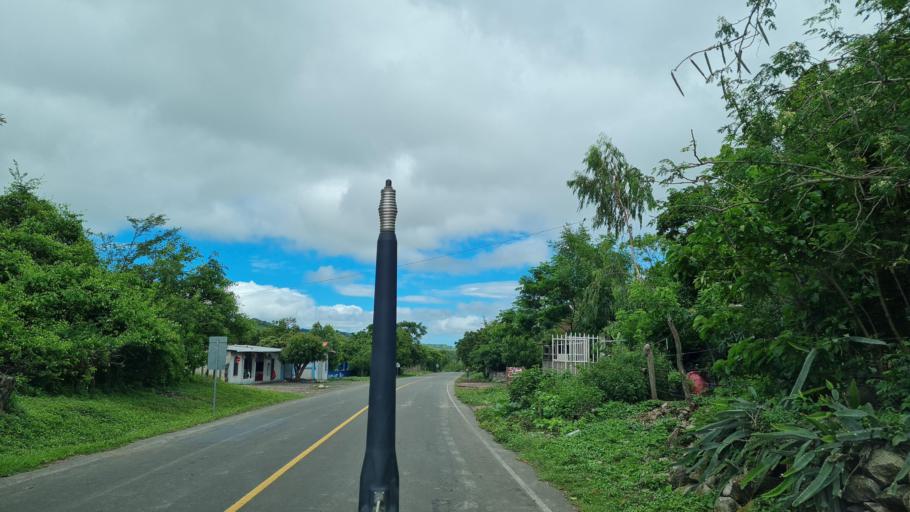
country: NI
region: Matagalpa
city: Terrabona
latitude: 12.5858
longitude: -85.9690
